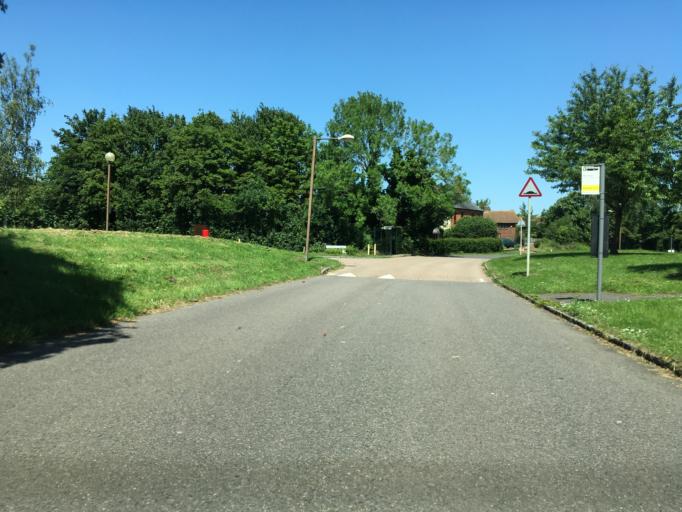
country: GB
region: England
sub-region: Milton Keynes
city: Simpson
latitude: 52.0317
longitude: -0.7245
